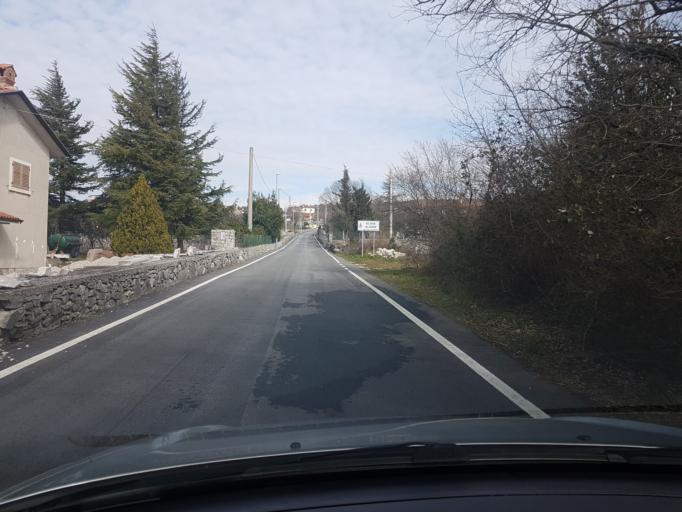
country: IT
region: Friuli Venezia Giulia
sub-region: Provincia di Trieste
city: Aurisina Cave
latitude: 45.7680
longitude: 13.6645
